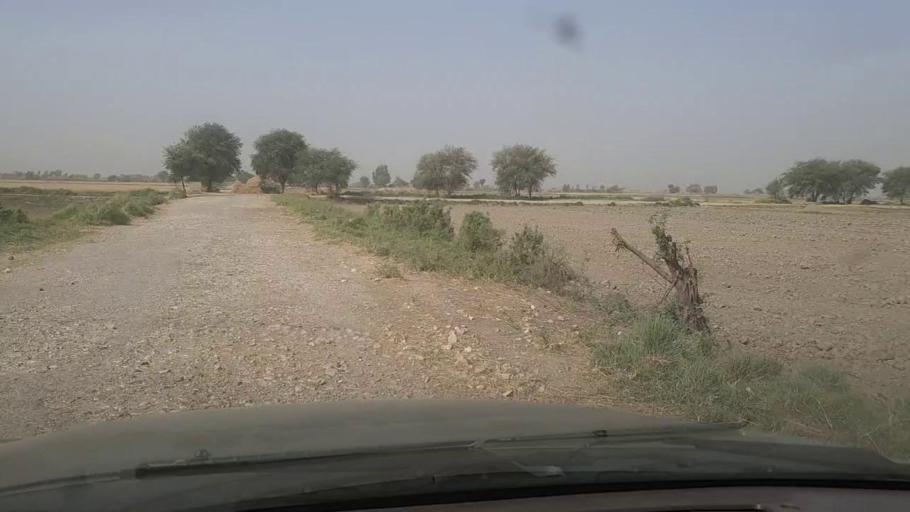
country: PK
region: Sindh
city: Garhi Yasin
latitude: 27.8887
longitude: 68.5776
